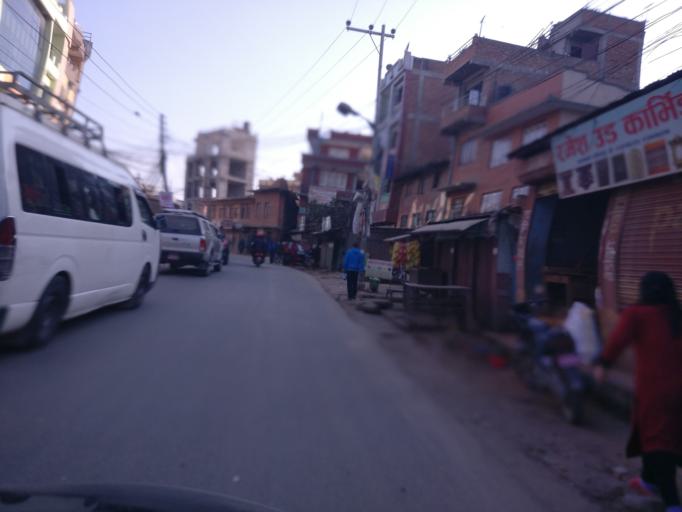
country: NP
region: Central Region
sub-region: Bagmati Zone
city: Patan
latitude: 27.6596
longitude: 85.3241
